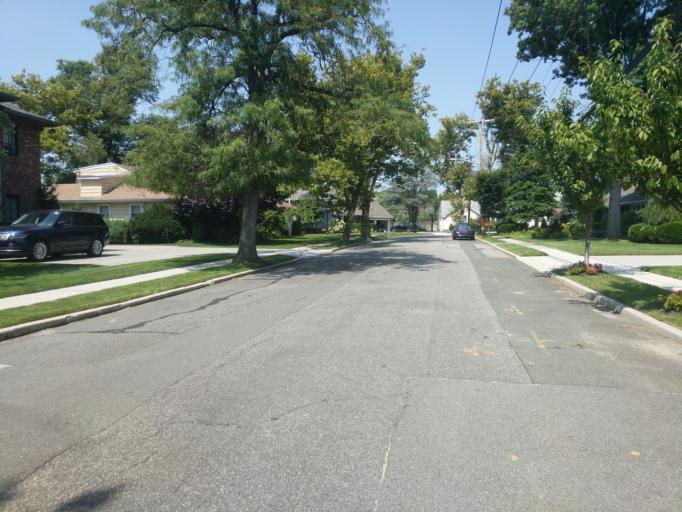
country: US
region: New York
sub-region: Nassau County
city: Woodmere
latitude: 40.6411
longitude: -73.7228
